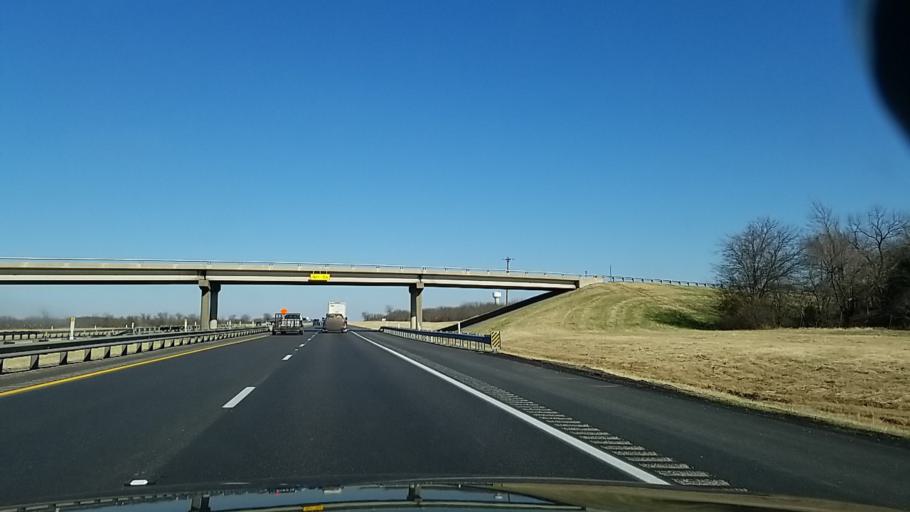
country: US
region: Texas
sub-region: Denton County
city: Argyle
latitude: 33.1176
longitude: -97.2150
